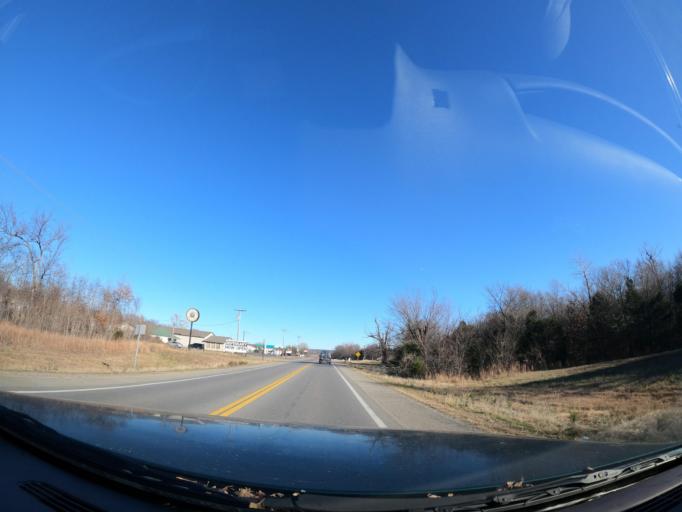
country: US
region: Oklahoma
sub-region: Pittsburg County
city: Longtown
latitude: 35.2392
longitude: -95.5148
